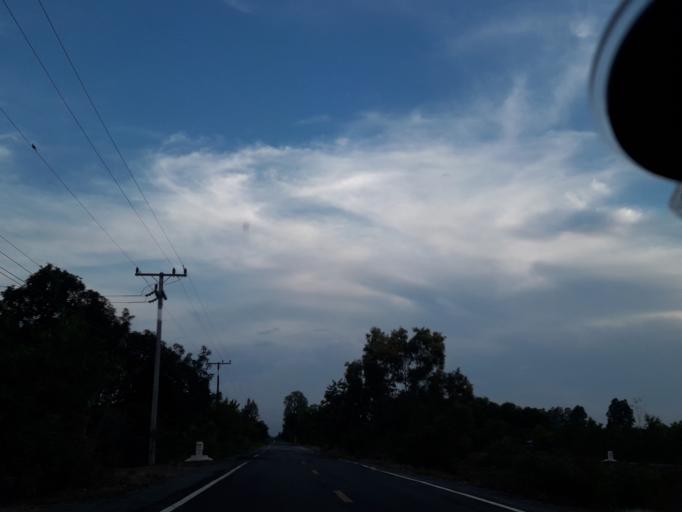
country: TH
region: Sara Buri
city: Nong Khae
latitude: 14.2592
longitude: 100.8688
